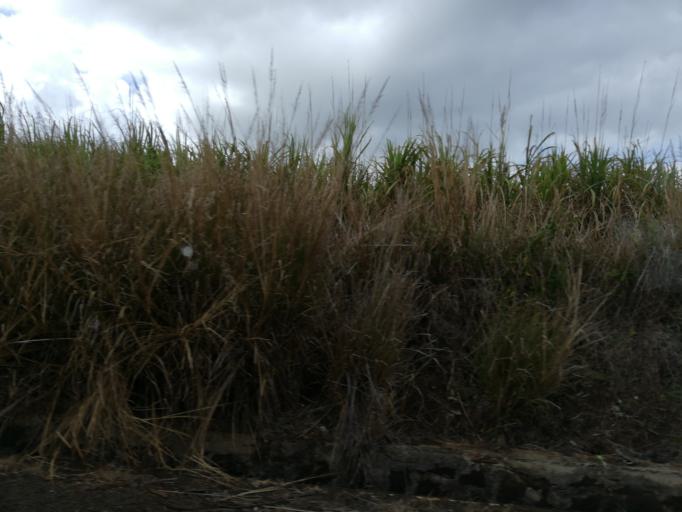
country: MU
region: Pamplemousses
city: Arsenal
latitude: -20.0961
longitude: 57.5420
